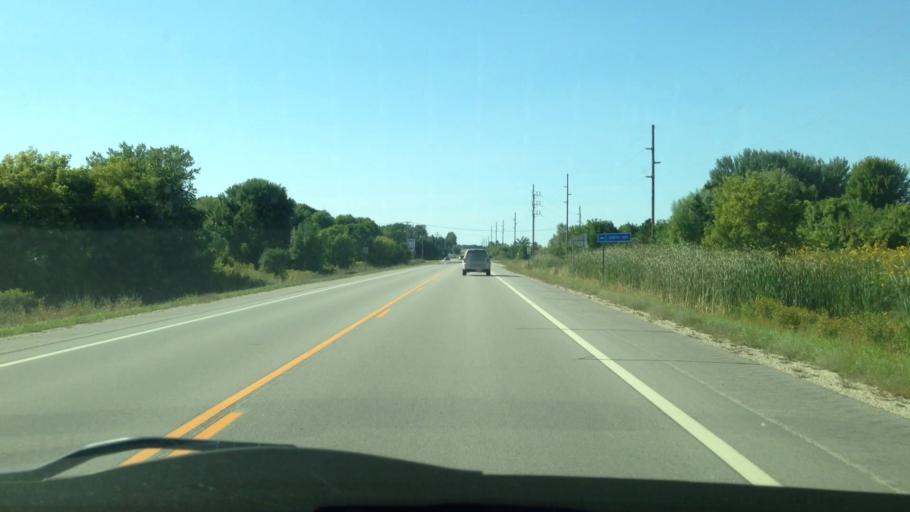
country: US
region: Minnesota
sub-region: Olmsted County
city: Eyota
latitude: 43.9898
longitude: -92.2261
